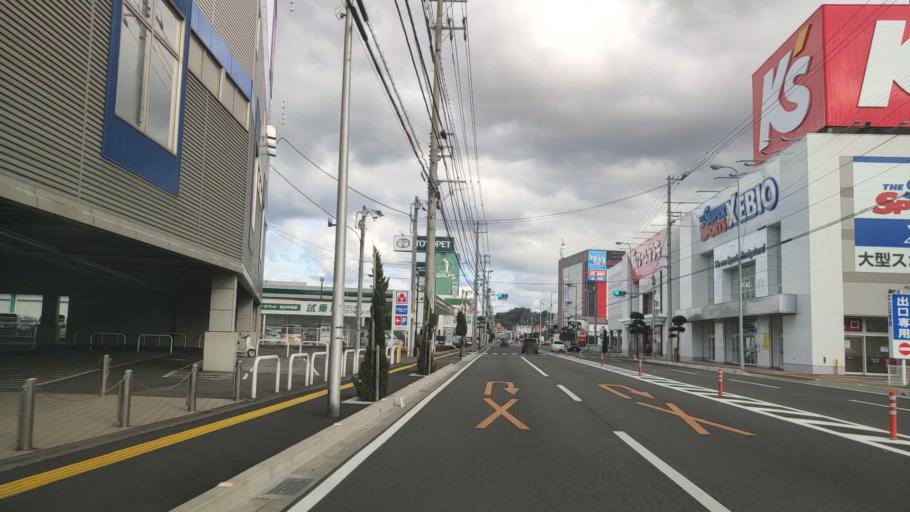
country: JP
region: Ehime
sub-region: Shikoku-chuo Shi
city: Matsuyama
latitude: 33.8643
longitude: 132.7504
